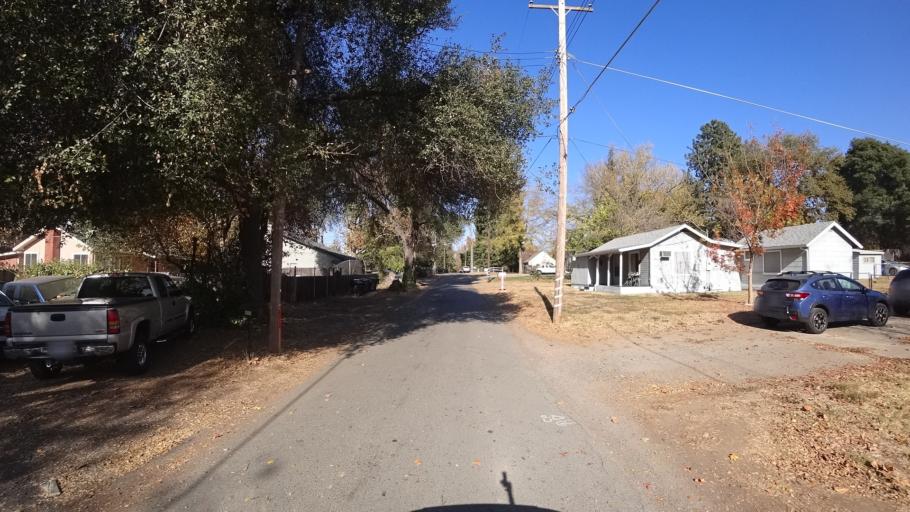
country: US
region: California
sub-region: Sacramento County
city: Citrus Heights
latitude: 38.6995
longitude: -121.2853
